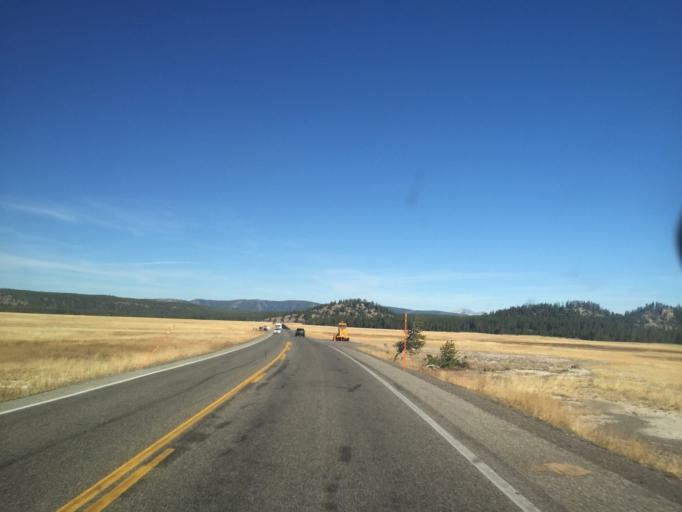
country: US
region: Montana
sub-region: Gallatin County
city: West Yellowstone
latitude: 44.5574
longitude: -110.8082
